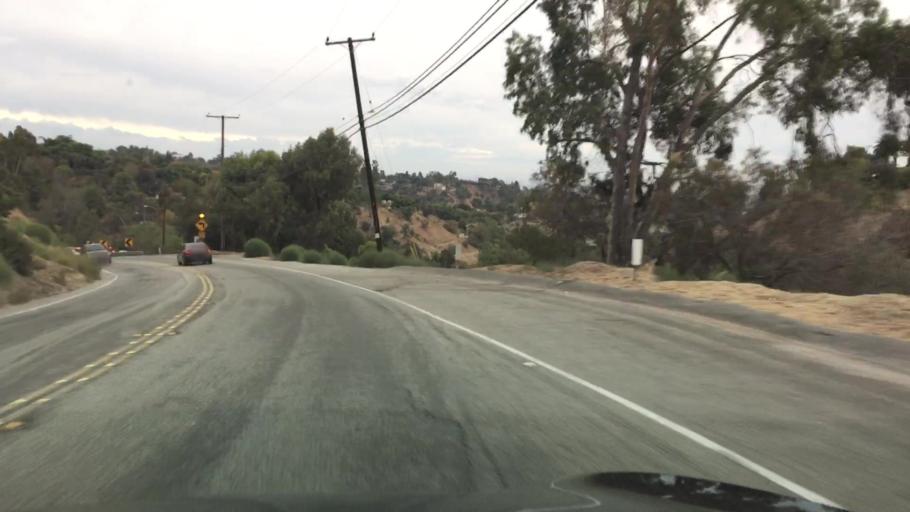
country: US
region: California
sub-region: Los Angeles County
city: La Habra Heights
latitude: 33.9674
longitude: -117.9609
